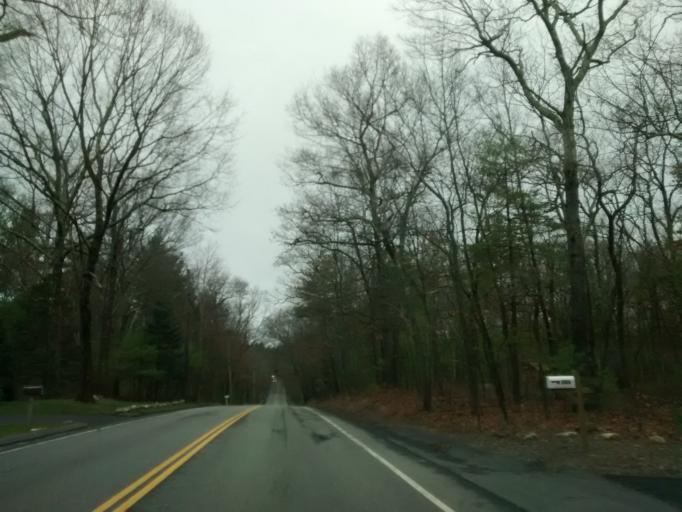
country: US
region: Massachusetts
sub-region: Worcester County
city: Upton
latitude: 42.1968
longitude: -71.5749
